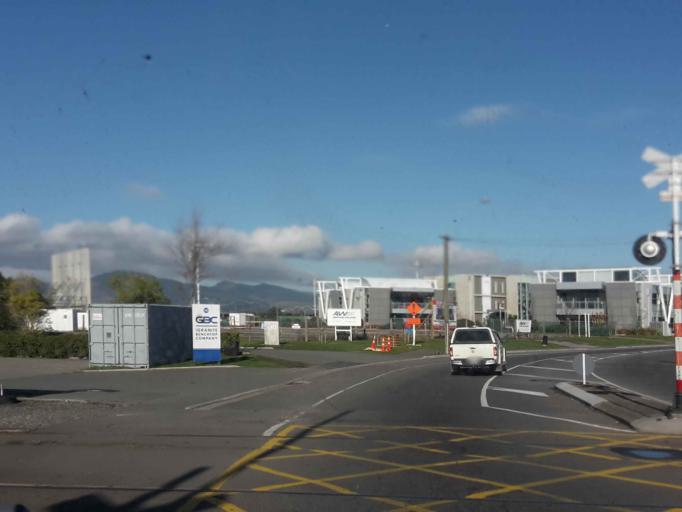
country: NZ
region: Canterbury
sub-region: Christchurch City
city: Christchurch
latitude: -43.5408
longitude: 172.5971
